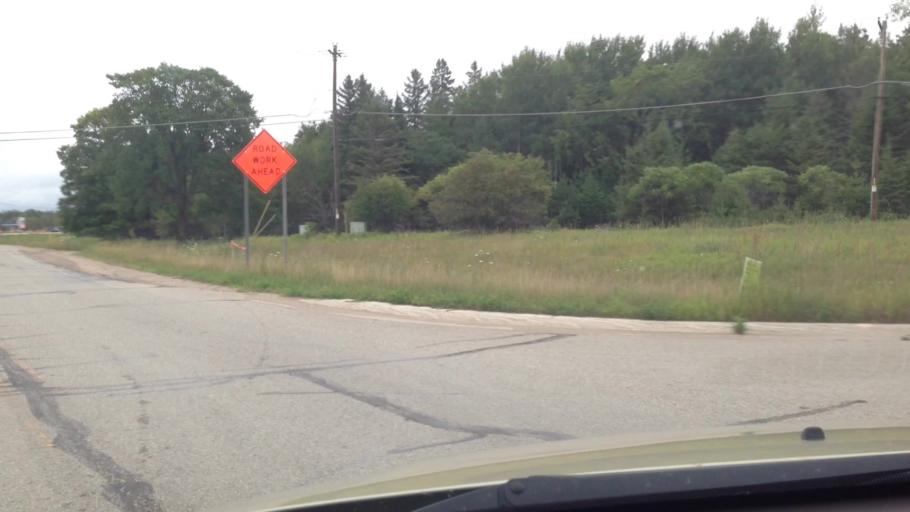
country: US
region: Michigan
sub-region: Delta County
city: Gladstone
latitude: 45.9251
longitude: -86.9815
